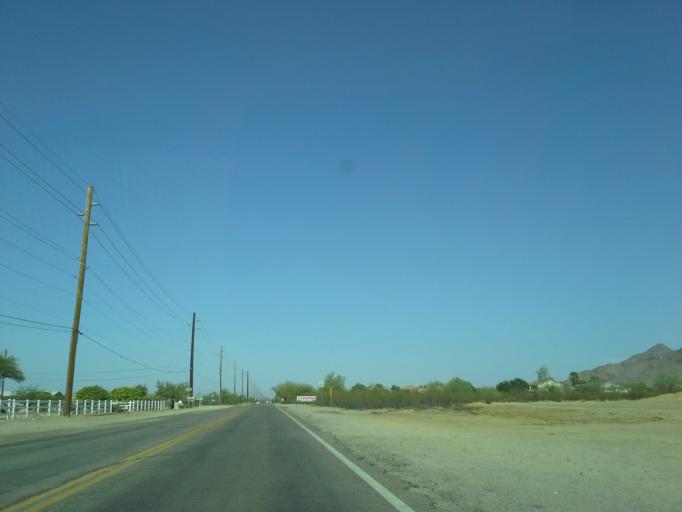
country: US
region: Arizona
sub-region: Maricopa County
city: Queen Creek
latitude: 33.2047
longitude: -111.6682
